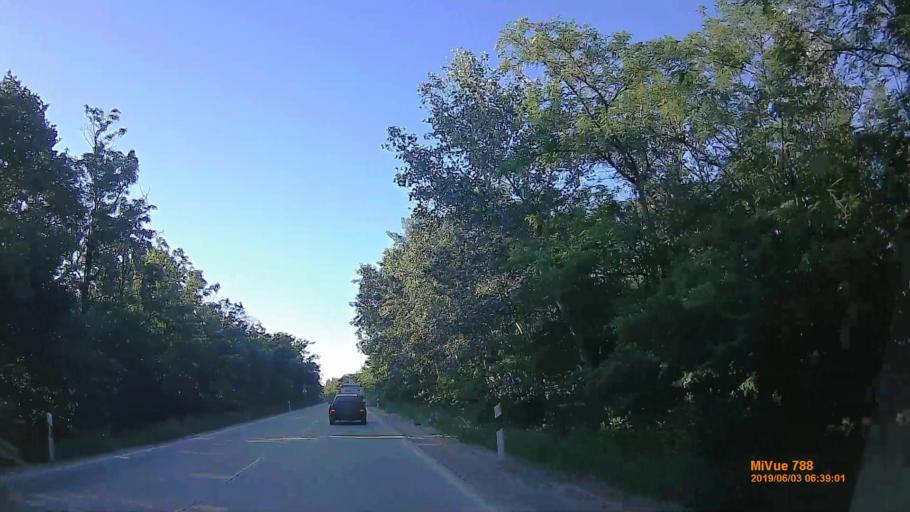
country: HU
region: Pest
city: Dunavarsany
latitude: 47.2906
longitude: 19.0964
